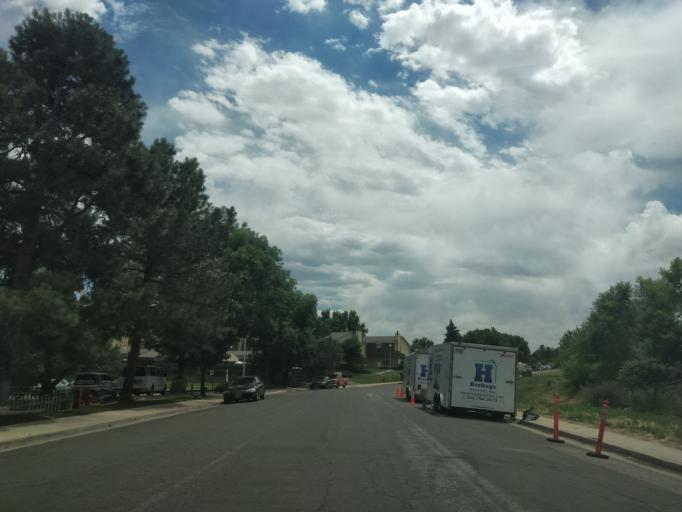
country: US
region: Colorado
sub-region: Jefferson County
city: Lakewood
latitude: 39.6913
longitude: -105.1221
